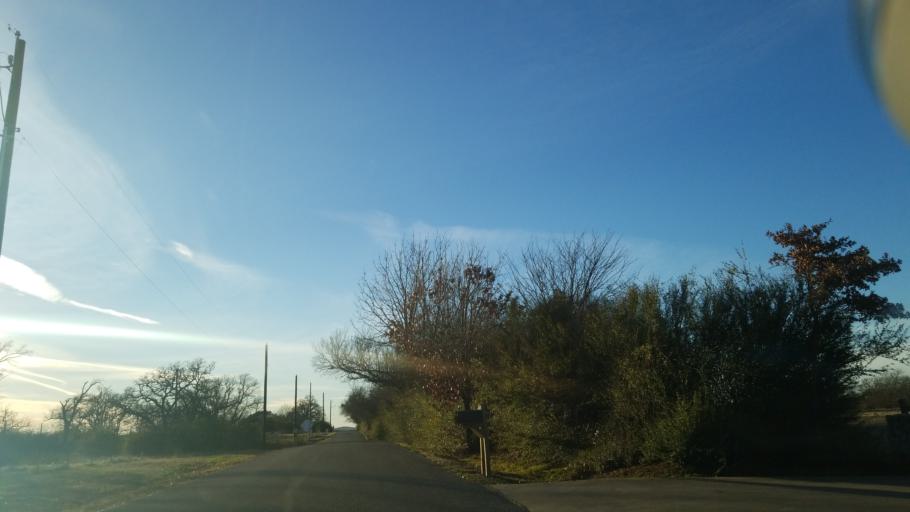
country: US
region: Texas
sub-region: Denton County
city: Denton
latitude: 33.1839
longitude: -97.1598
